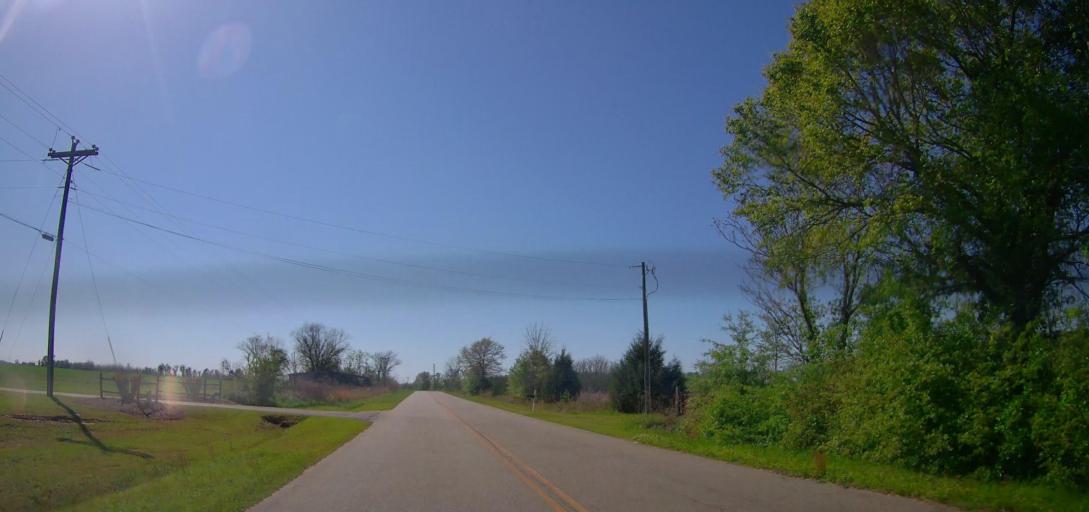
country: US
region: Georgia
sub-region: Pulaski County
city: Hawkinsville
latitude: 32.2441
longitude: -83.5683
